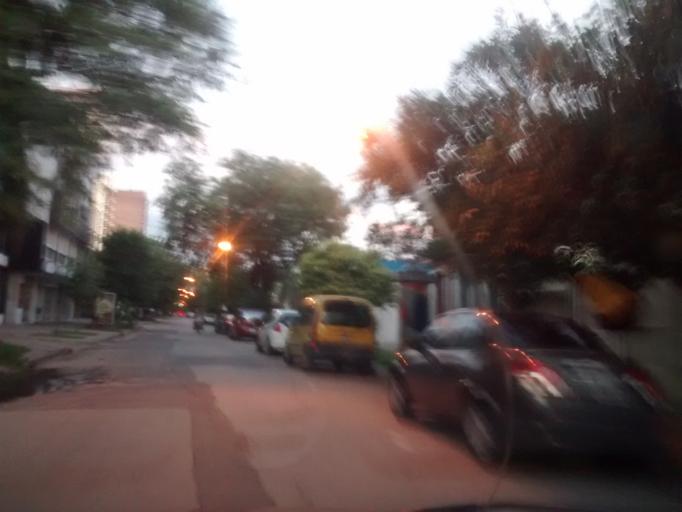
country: AR
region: Chaco
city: Resistencia
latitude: -27.4571
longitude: -58.9879
